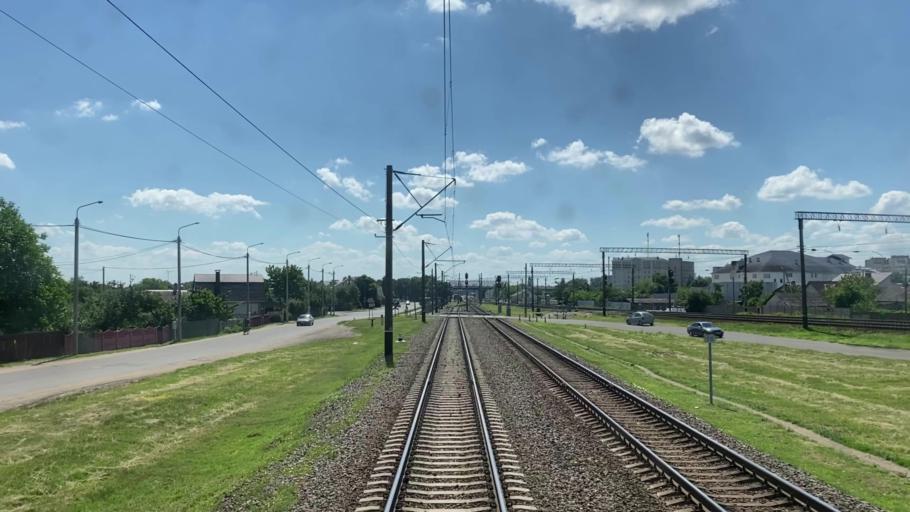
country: BY
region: Brest
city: Baranovichi
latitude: 53.1378
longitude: 26.0330
